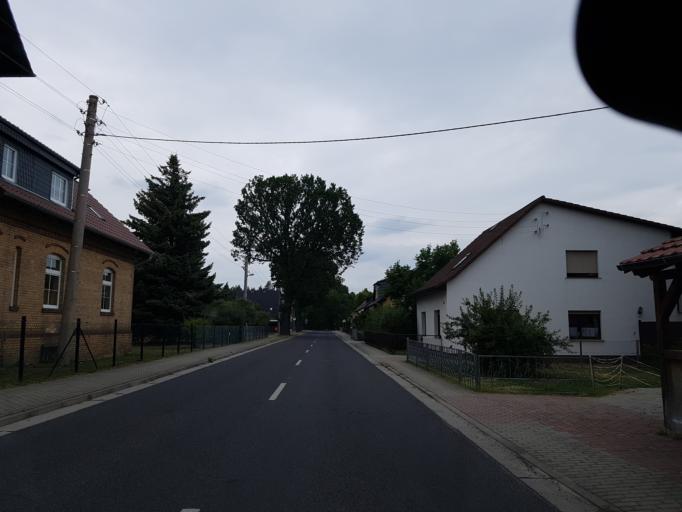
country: DE
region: Brandenburg
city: Sallgast
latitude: 51.5909
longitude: 13.8458
